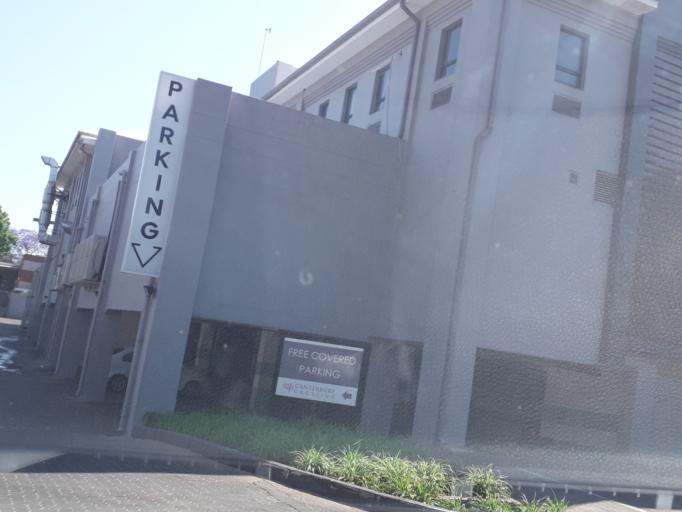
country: ZA
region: Gauteng
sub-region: City of Johannesburg Metropolitan Municipality
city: Johannesburg
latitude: -26.1071
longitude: 28.0007
